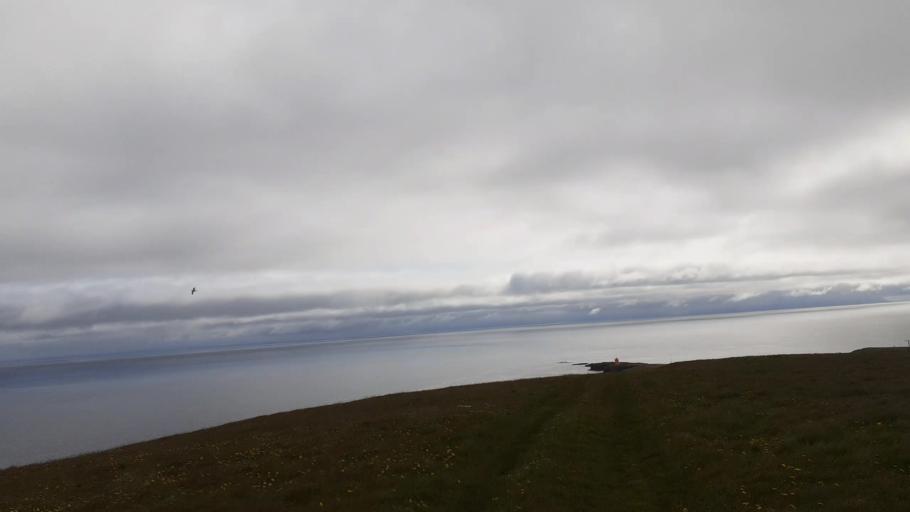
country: IS
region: Northeast
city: Dalvik
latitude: 66.5370
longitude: -17.9814
